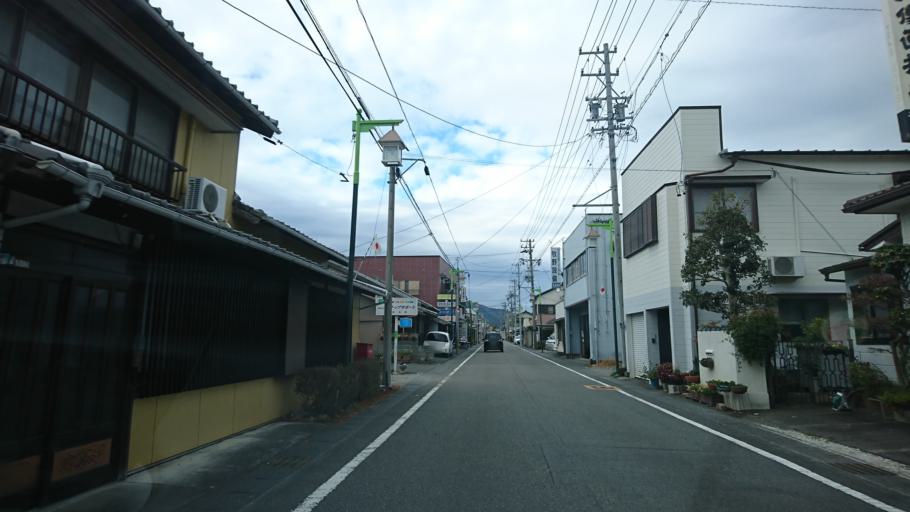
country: JP
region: Shizuoka
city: Kanaya
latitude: 34.8308
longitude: 138.1274
